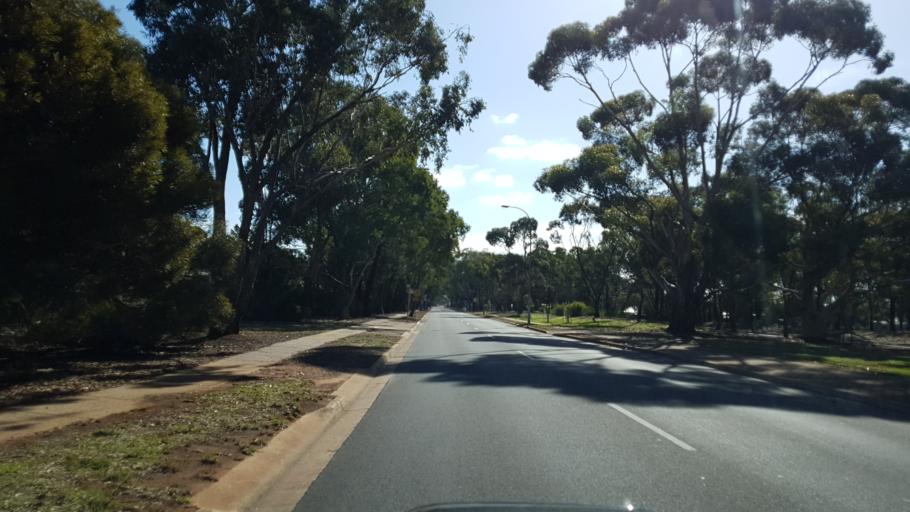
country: AU
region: South Australia
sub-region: Salisbury
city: Salisbury
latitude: -34.7384
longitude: 138.6238
